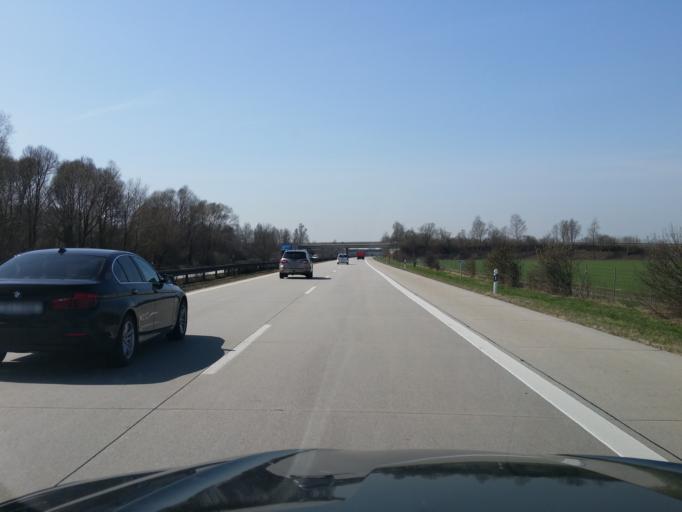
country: DE
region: Bavaria
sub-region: Upper Bavaria
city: Langenpreising
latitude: 48.4281
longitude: 11.9392
